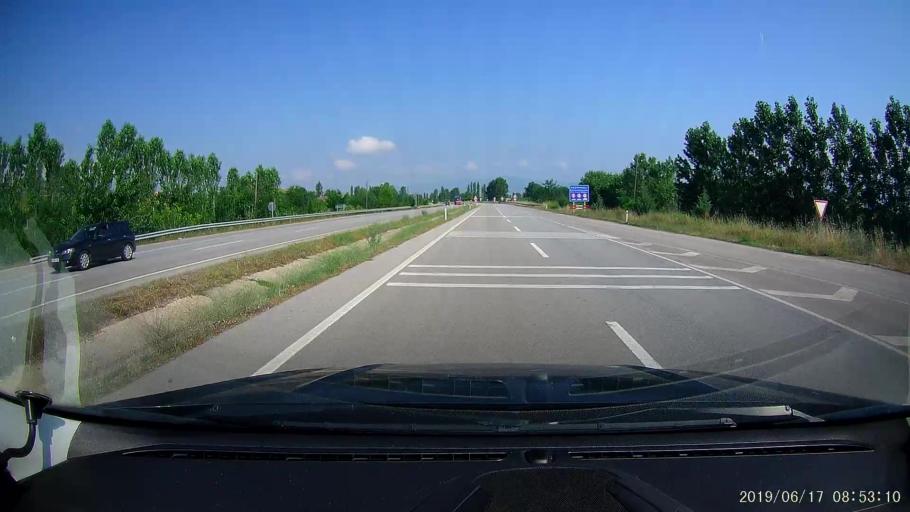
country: TR
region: Tokat
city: Erbaa
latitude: 40.7070
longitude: 36.4856
